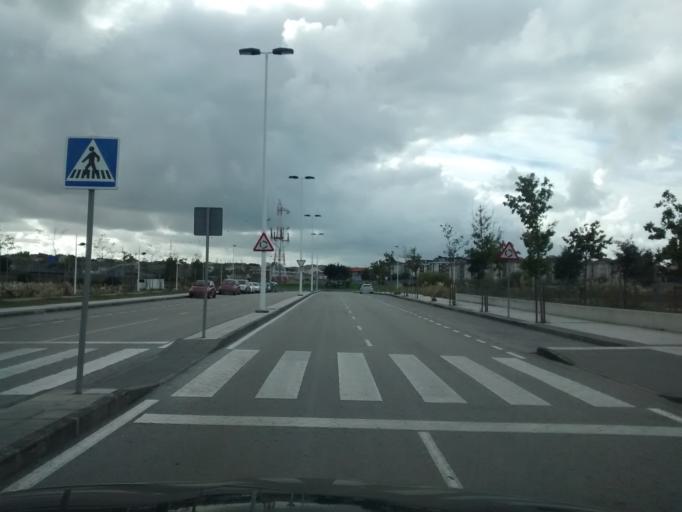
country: ES
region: Cantabria
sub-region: Provincia de Cantabria
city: Camargo
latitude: 43.4392
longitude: -3.8570
